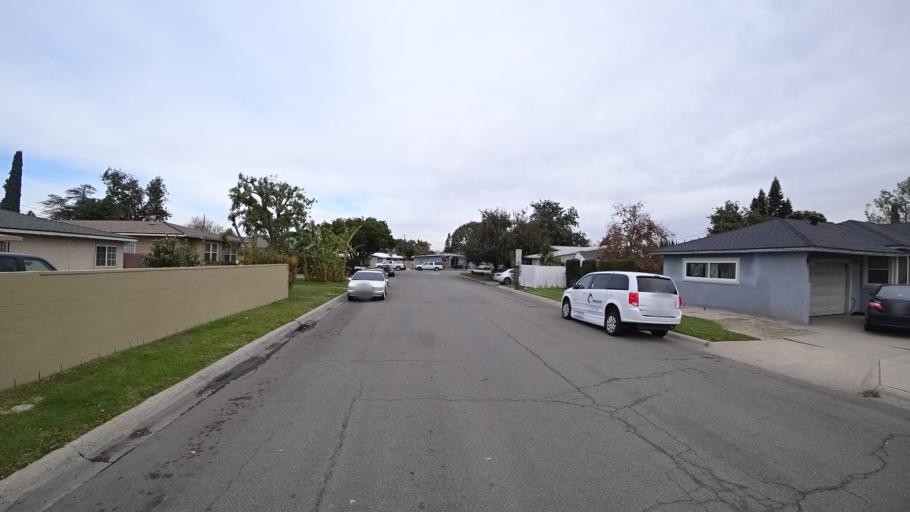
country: US
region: California
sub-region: Orange County
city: Garden Grove
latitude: 33.7707
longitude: -117.9349
